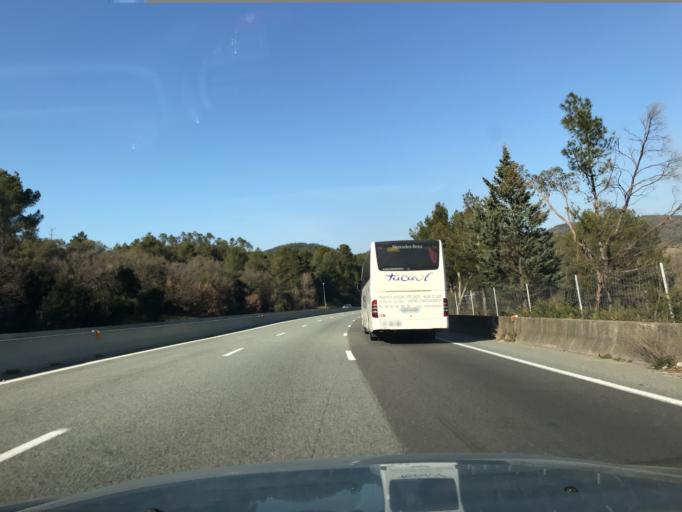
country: FR
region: Provence-Alpes-Cote d'Azur
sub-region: Departement du Var
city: Frejus
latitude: 43.4826
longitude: 6.7393
